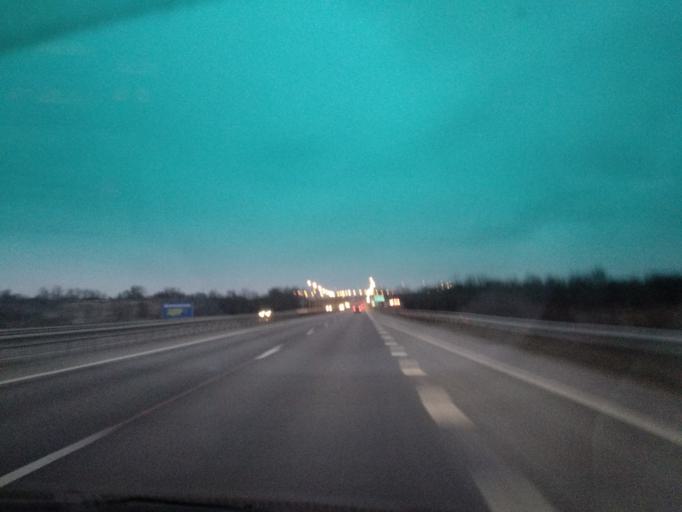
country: RU
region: Adygeya
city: Adygeysk
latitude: 44.8326
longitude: 39.2190
